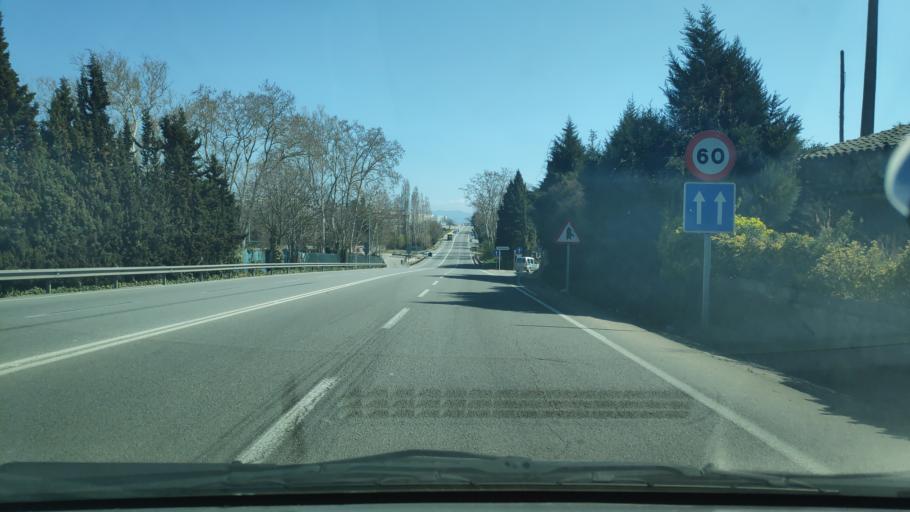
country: ES
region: Catalonia
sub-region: Provincia de Barcelona
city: Polinya
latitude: 41.5332
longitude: 2.1540
